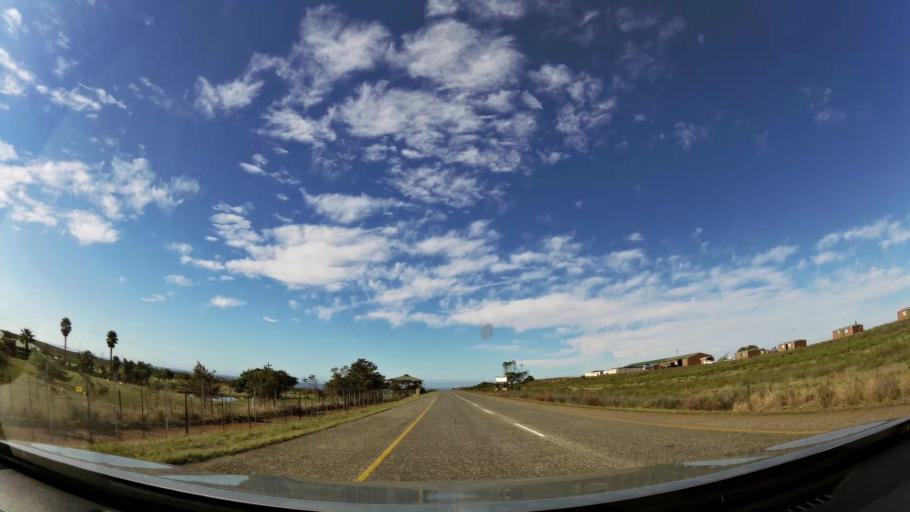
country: ZA
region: Eastern Cape
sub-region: Cacadu District Municipality
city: Jeffrey's Bay
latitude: -34.0176
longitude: 24.8890
